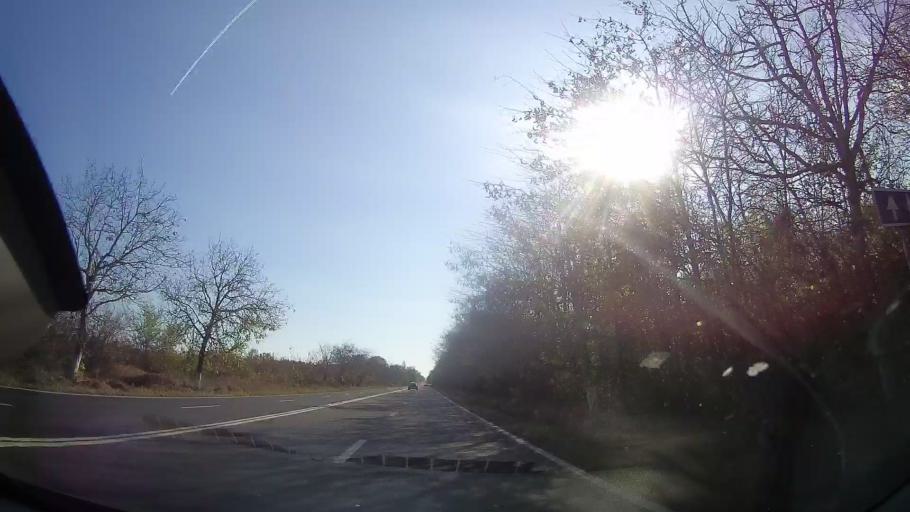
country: RO
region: Constanta
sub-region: Comuna Douazeci si Trei August
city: Dulcesti
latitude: 43.8803
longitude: 28.5735
